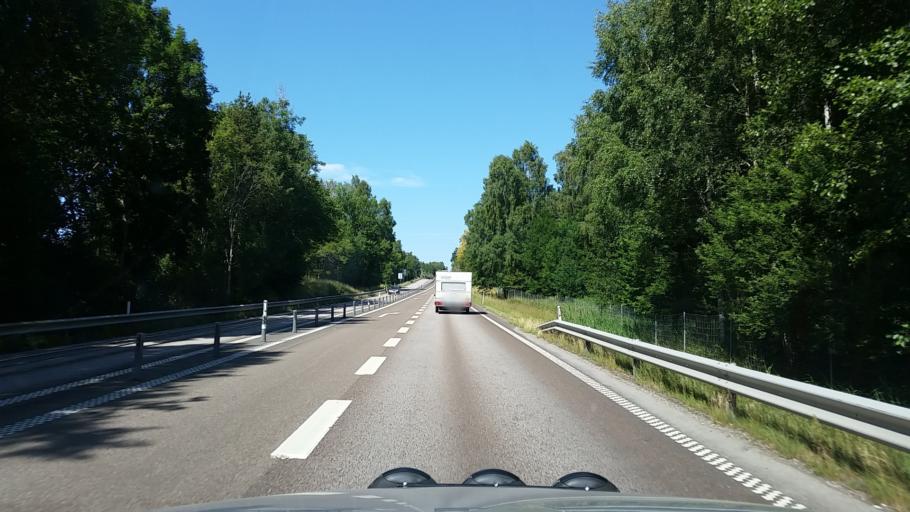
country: SE
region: Vaestra Goetaland
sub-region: Melleruds Kommun
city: Mellerud
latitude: 58.8151
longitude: 12.5236
